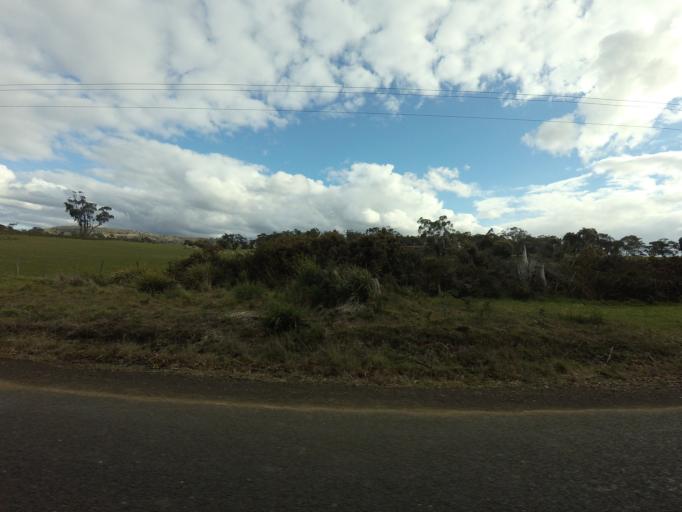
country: AU
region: Tasmania
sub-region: Northern Midlands
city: Evandale
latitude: -41.8744
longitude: 147.3019
